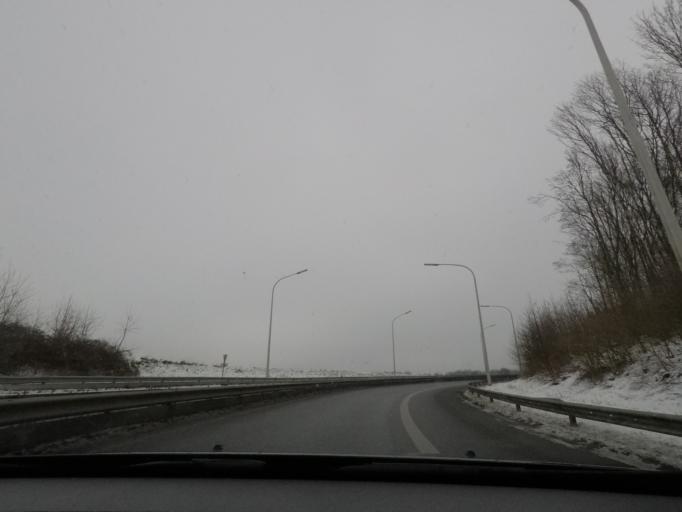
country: BE
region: Wallonia
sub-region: Province de Namur
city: Sombreffe
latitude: 50.4885
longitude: 4.6006
